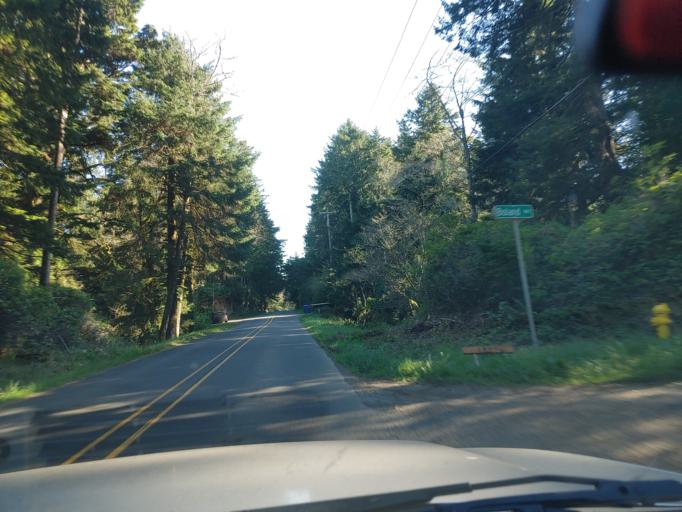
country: US
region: Oregon
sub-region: Lincoln County
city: Depoe Bay
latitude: 44.7443
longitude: -124.0559
